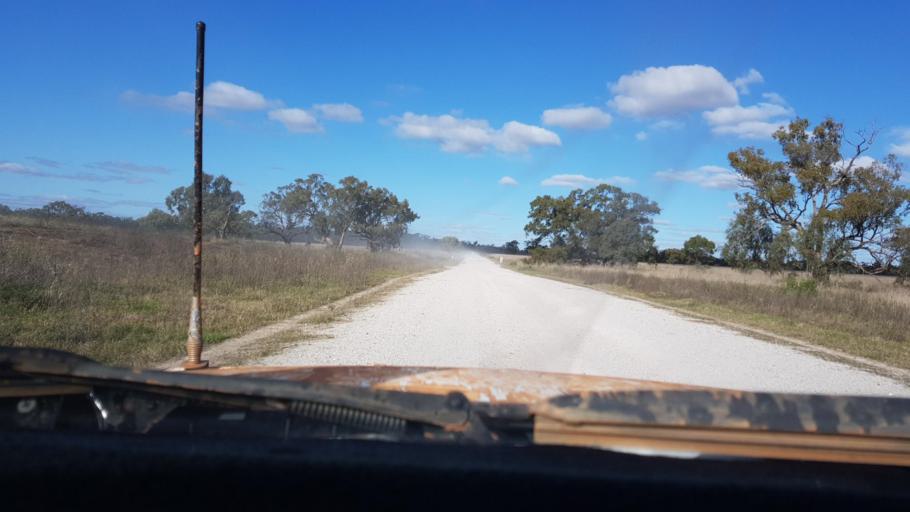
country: AU
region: New South Wales
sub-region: Lachlan
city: Condobolin
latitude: -33.1298
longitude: 147.2622
